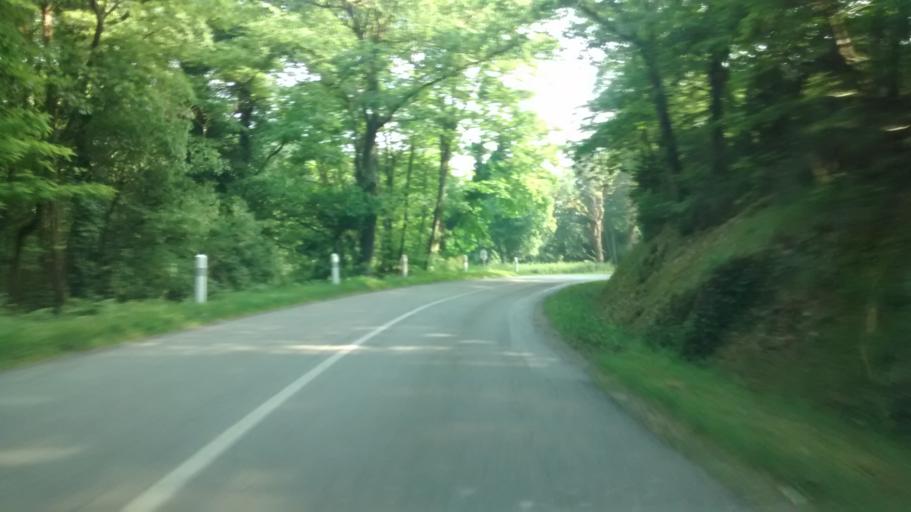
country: FR
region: Brittany
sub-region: Departement du Morbihan
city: Guer
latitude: 47.8939
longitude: -2.1521
